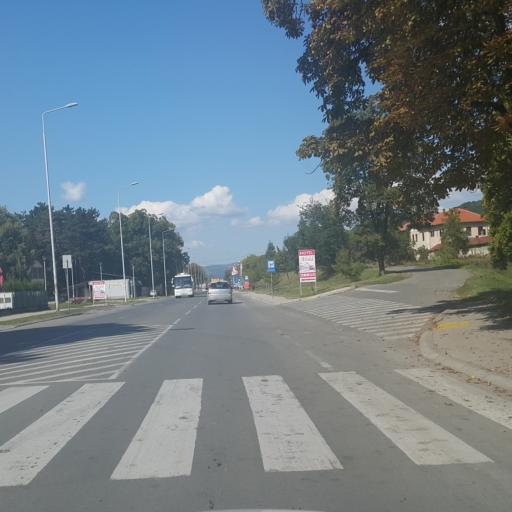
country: RS
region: Central Serbia
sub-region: Pirotski Okrug
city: Pirot
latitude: 43.1681
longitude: 22.5870
